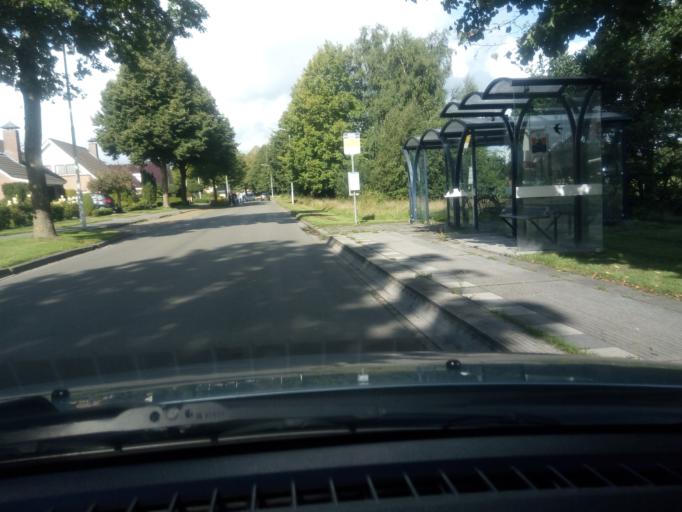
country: NL
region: Friesland
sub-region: Gemeente Achtkarspelen
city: Surhuisterveen
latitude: 53.1852
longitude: 6.1800
